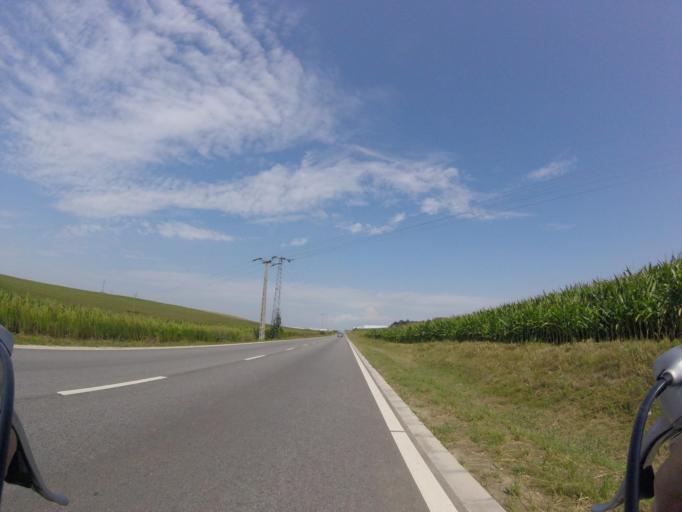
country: HU
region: Komarom-Esztergom
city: Tatabanya
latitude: 47.5758
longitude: 18.3586
